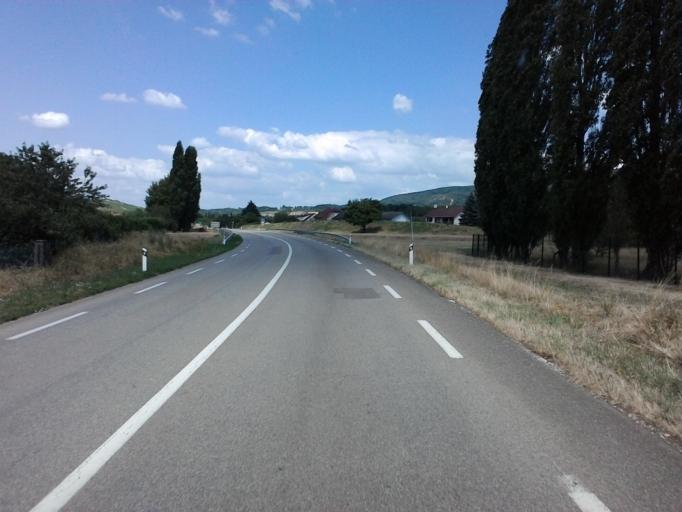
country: FR
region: Franche-Comte
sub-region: Departement du Jura
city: Poligny
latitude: 46.8378
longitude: 5.6968
